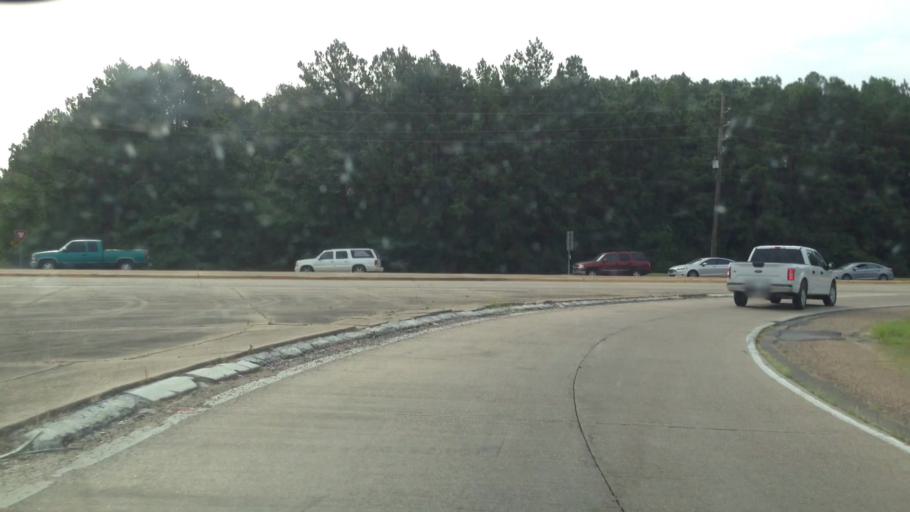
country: US
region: Louisiana
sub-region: Caddo Parish
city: Shreveport
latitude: 32.4165
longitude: -93.8153
